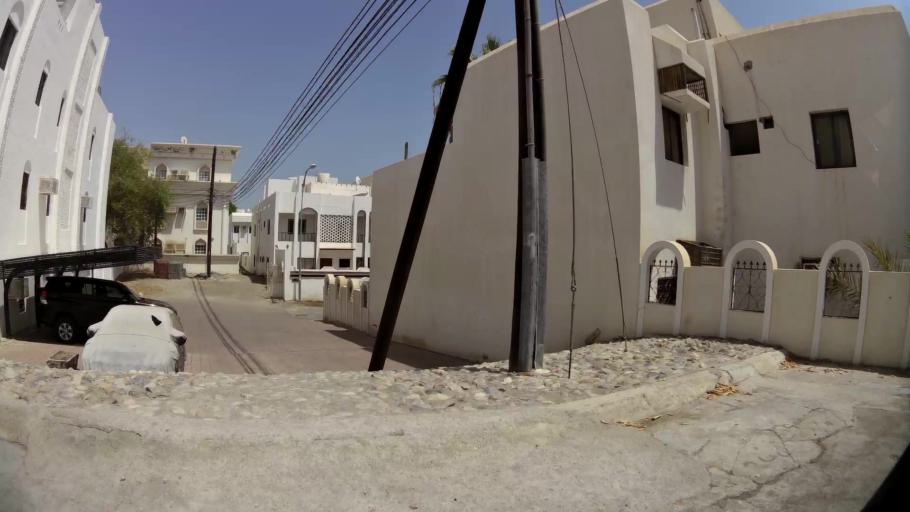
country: OM
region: Muhafazat Masqat
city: Bawshar
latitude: 23.5914
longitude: 58.4348
